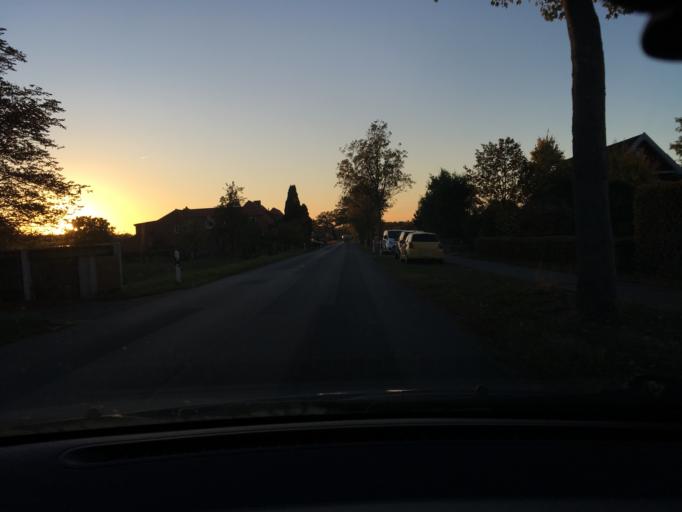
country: DE
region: Lower Saxony
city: Bleckede
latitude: 53.3085
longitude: 10.6875
